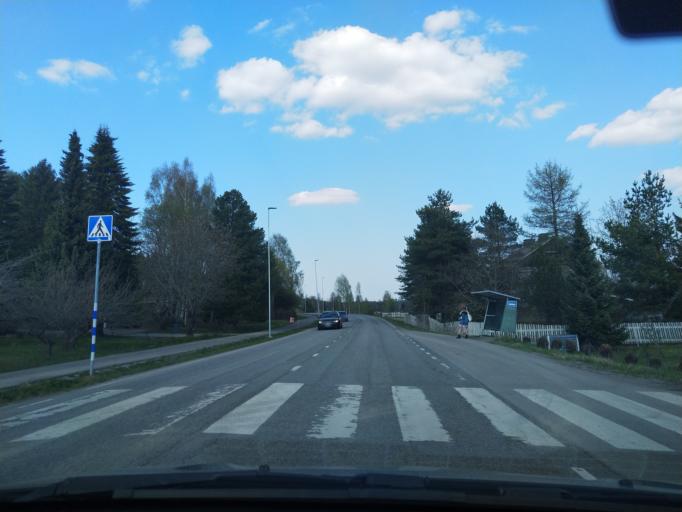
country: FI
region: Uusimaa
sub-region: Helsinki
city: Lohja
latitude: 60.2012
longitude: 24.0062
